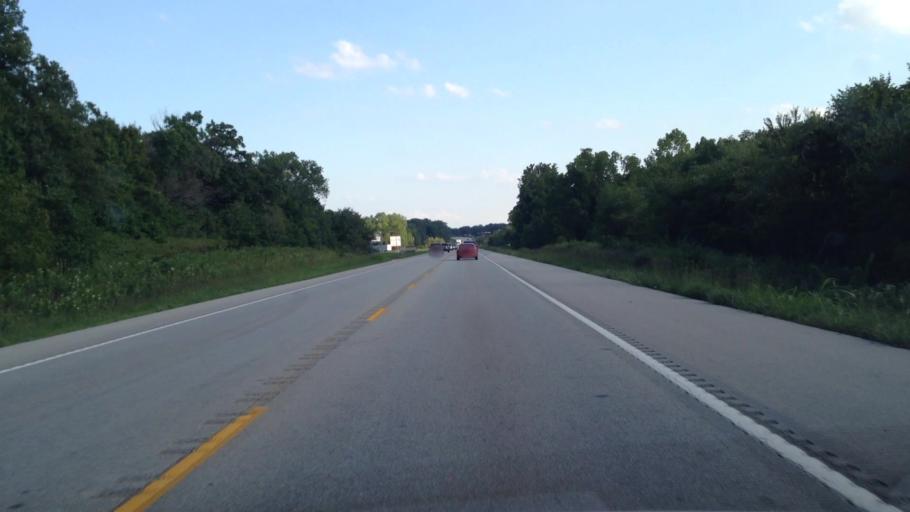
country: US
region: Missouri
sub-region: Jasper County
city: Carl Junction
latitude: 37.1549
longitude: -94.5271
